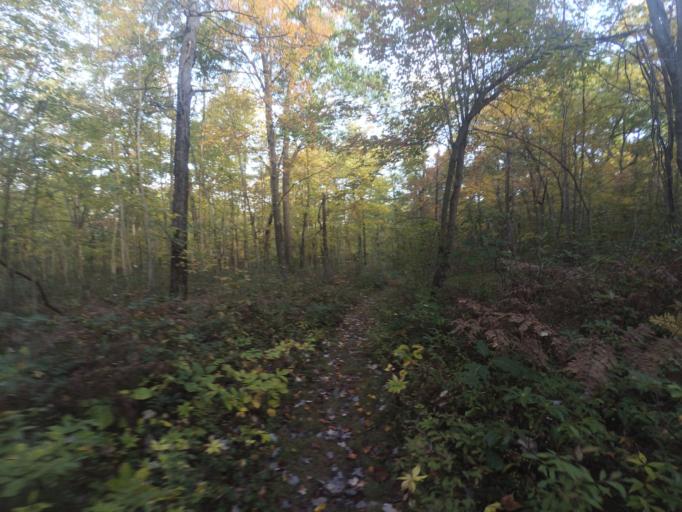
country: US
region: Pennsylvania
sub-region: Centre County
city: Stormstown
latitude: 40.8926
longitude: -78.0014
